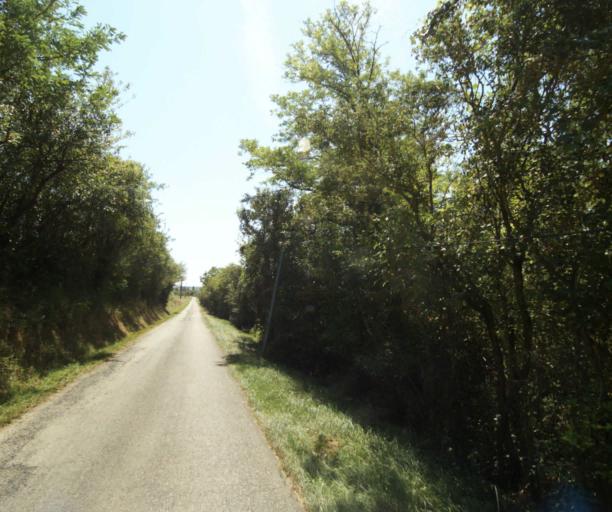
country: FR
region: Midi-Pyrenees
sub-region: Departement de la Haute-Garonne
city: Saint-Sulpice-sur-Leze
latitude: 43.3125
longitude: 1.3386
